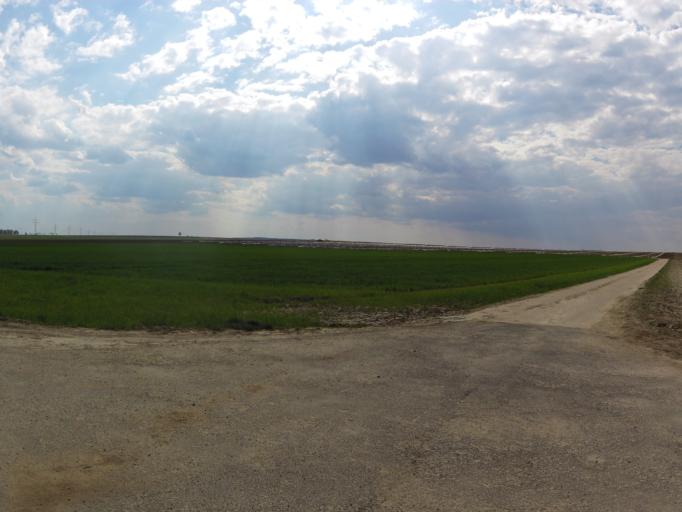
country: DE
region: Bavaria
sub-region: Regierungsbezirk Unterfranken
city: Oberpleichfeld
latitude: 49.8735
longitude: 10.0969
